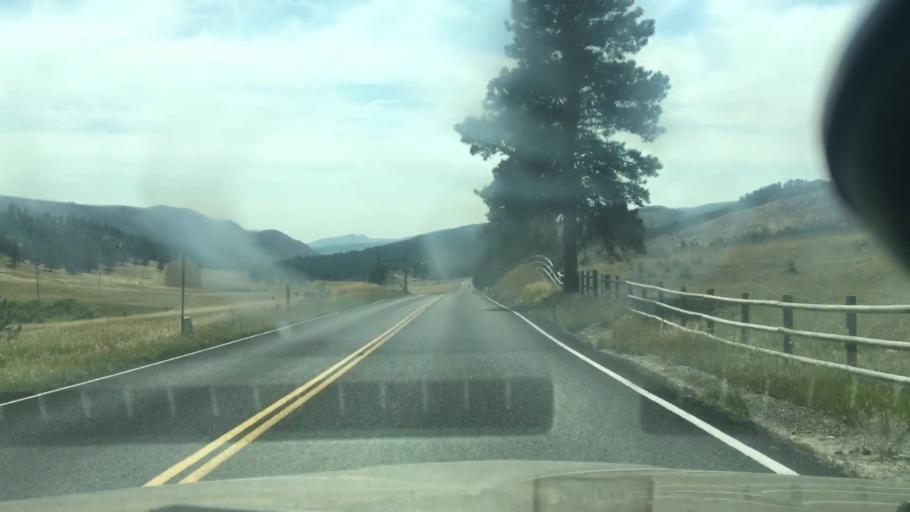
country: US
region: Colorado
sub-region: Larimer County
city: Laporte
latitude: 40.6179
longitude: -105.3571
